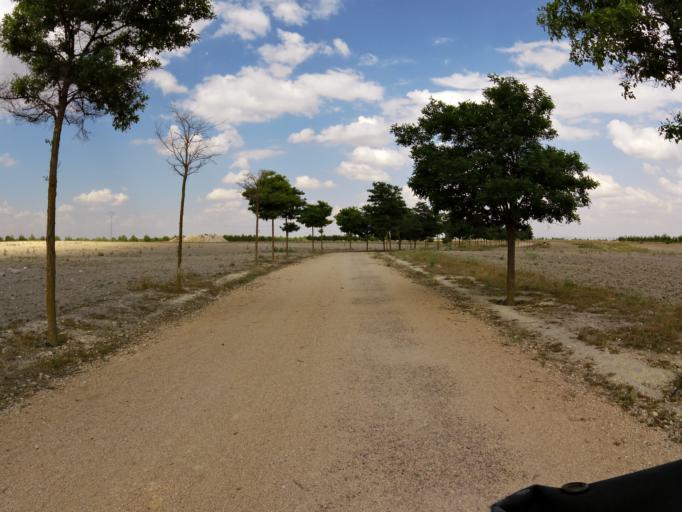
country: ES
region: Castille-La Mancha
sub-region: Provincia de Albacete
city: Albacete
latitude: 38.9581
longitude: -1.9756
